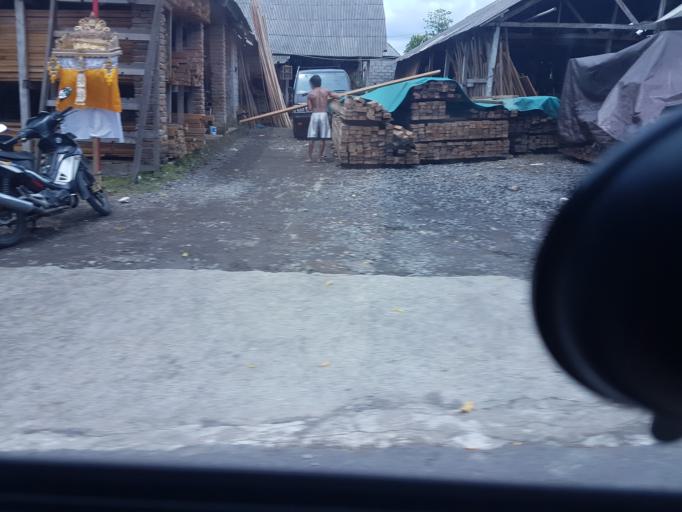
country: ID
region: Bali
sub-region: Kabupaten Gianyar
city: Ubud
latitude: -8.5205
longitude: 115.2931
